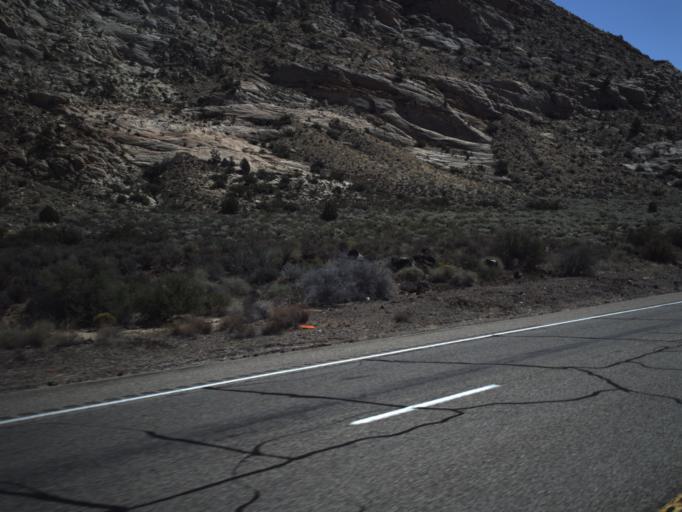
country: US
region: Utah
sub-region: Washington County
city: Ivins
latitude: 37.2356
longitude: -113.6353
